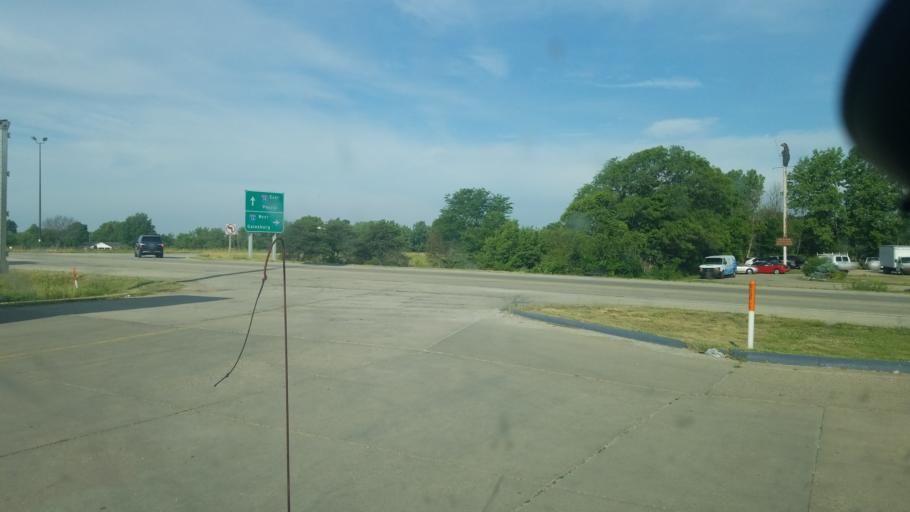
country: US
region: Illinois
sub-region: Peoria County
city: Hanna City
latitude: 40.7760
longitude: -89.7523
